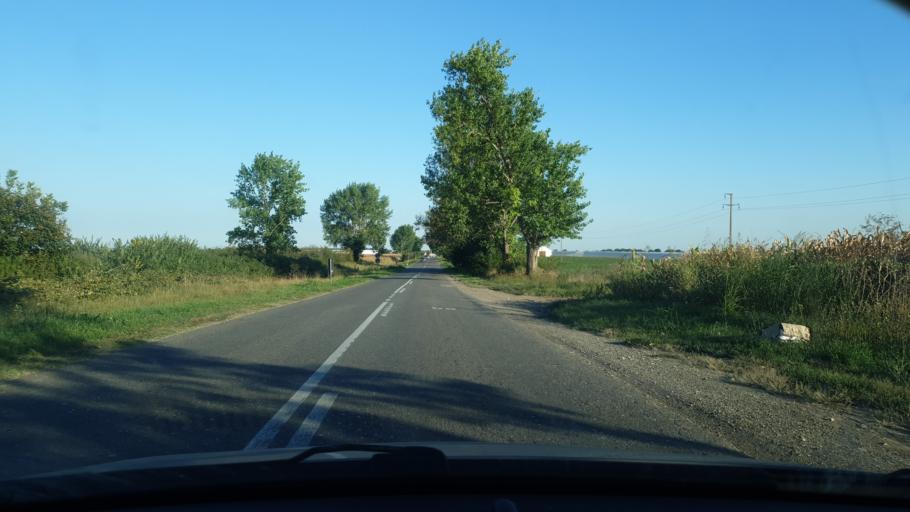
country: RS
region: Autonomna Pokrajina Vojvodina
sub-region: Sremski Okrug
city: Ruma
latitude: 44.9886
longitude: 19.8633
